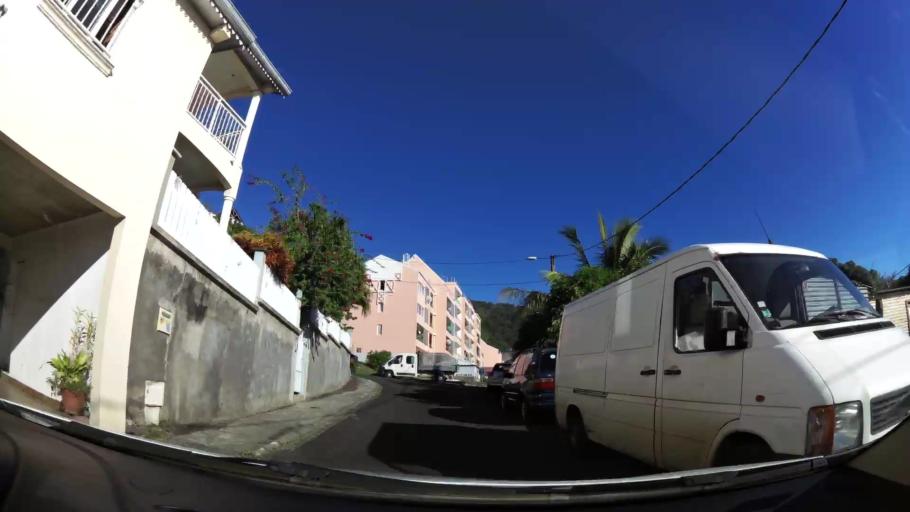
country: RE
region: Reunion
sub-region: Reunion
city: Saint-Denis
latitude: -20.8920
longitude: 55.4478
